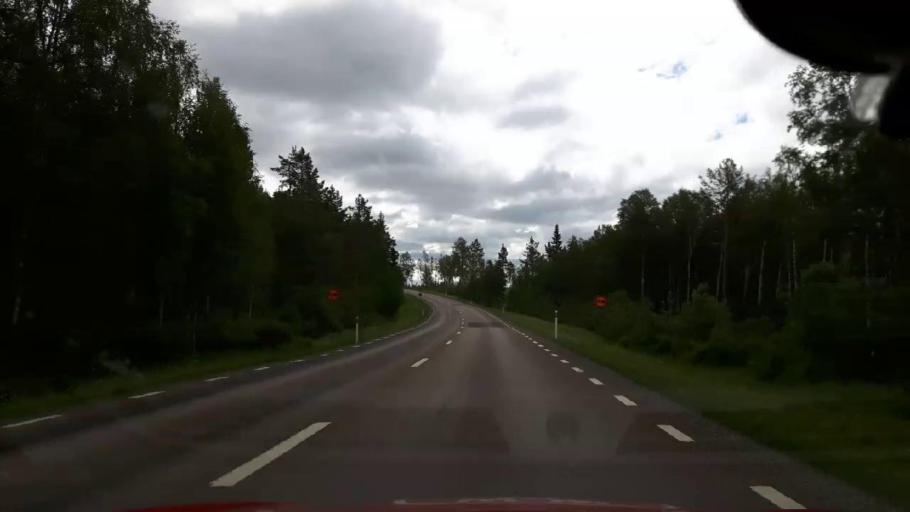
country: SE
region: Jaemtland
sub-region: OEstersunds Kommun
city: Brunflo
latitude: 63.0225
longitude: 14.9235
